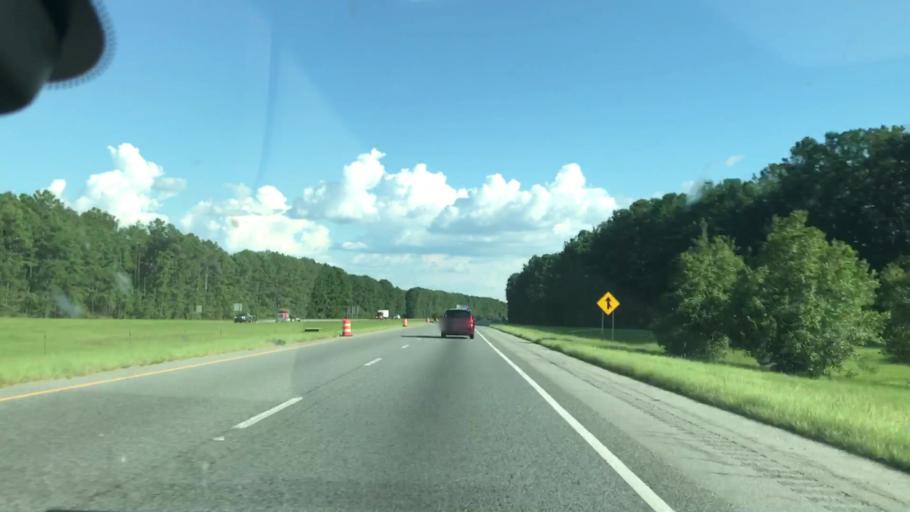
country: US
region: Georgia
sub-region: Harris County
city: Hamilton
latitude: 32.6605
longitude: -84.9792
